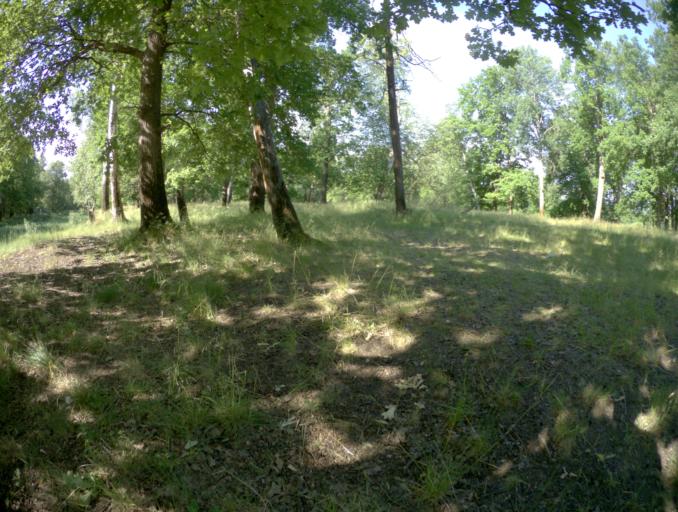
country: RU
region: Ivanovo
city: Talitsy
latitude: 56.5292
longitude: 42.3692
